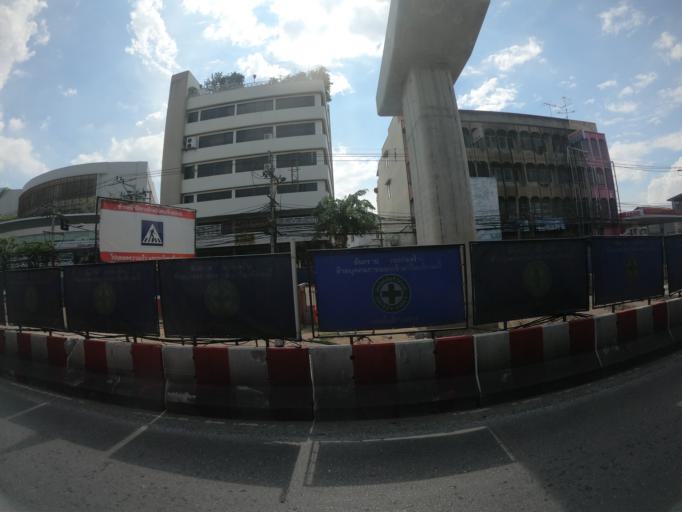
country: TH
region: Bangkok
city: Wang Thonglang
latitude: 13.7905
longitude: 100.6014
